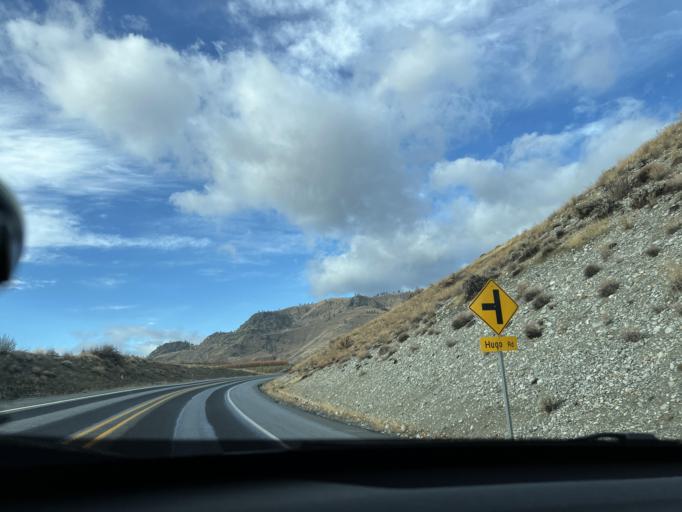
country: US
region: Washington
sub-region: Chelan County
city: Chelan
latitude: 47.8628
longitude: -119.9313
